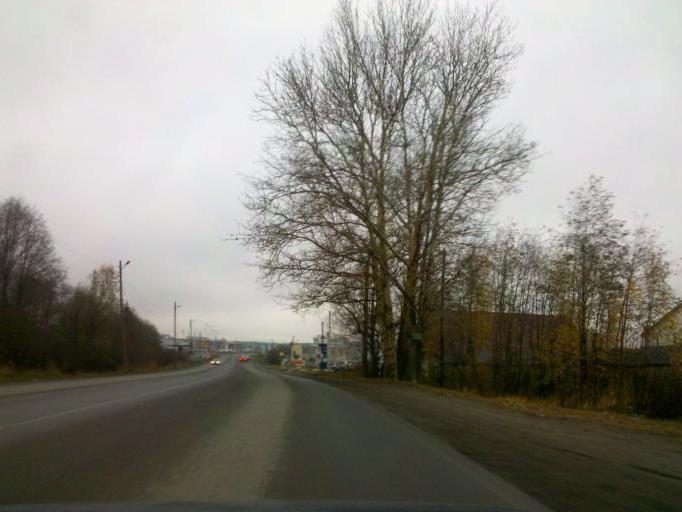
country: RU
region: Republic of Karelia
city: Petrozavodsk
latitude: 61.8159
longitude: 34.2836
